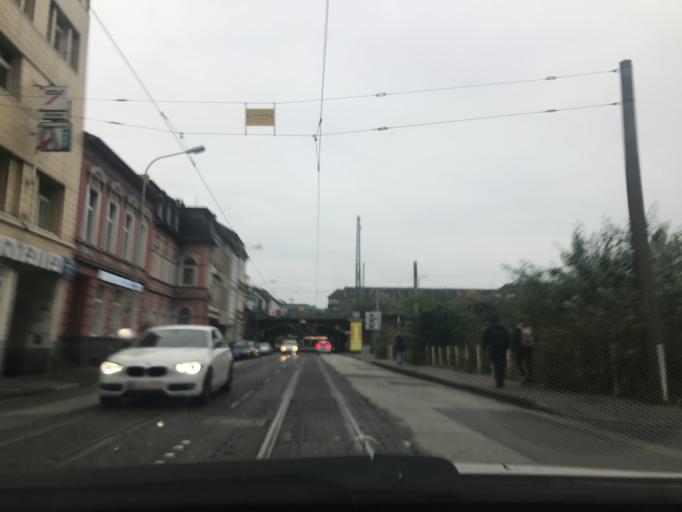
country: DE
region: North Rhine-Westphalia
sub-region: Regierungsbezirk Dusseldorf
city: Krefeld
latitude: 51.3241
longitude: 6.5686
